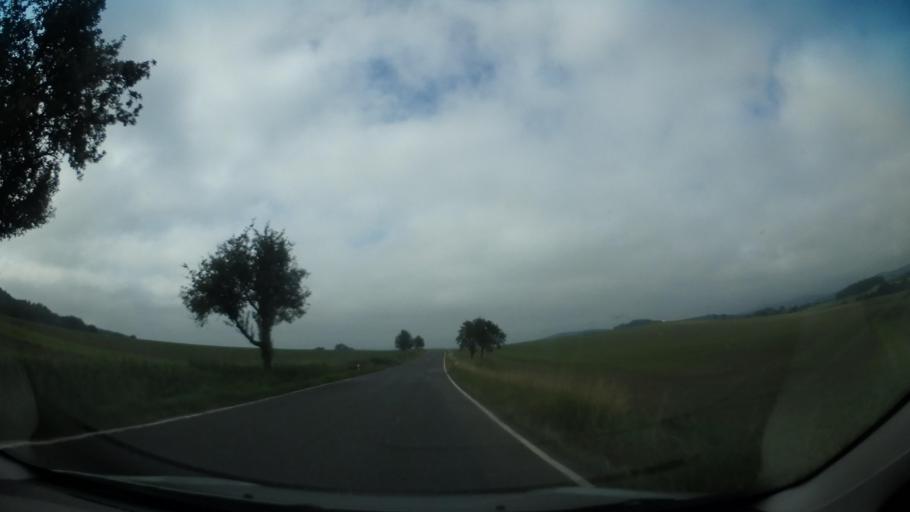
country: CZ
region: Central Bohemia
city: Sedlcany
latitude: 49.7050
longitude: 14.4475
